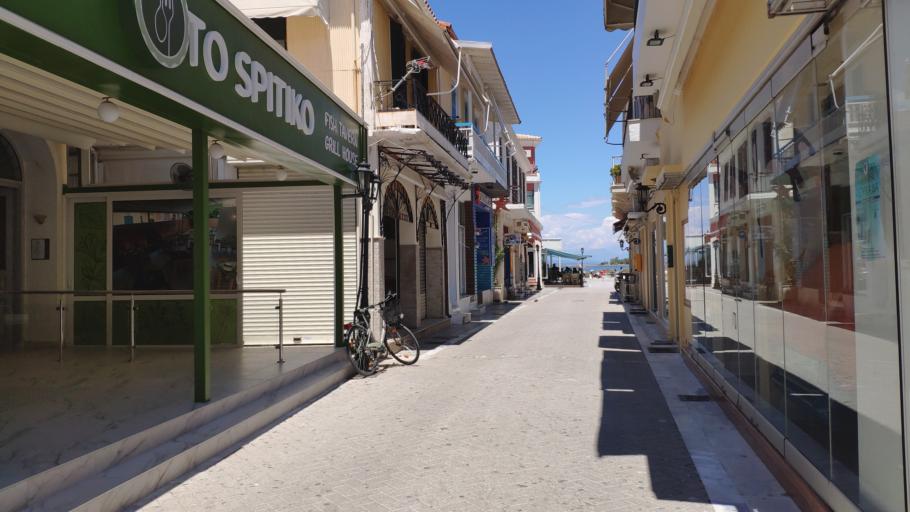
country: GR
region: Ionian Islands
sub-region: Lefkada
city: Lefkada
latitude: 38.8349
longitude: 20.7094
